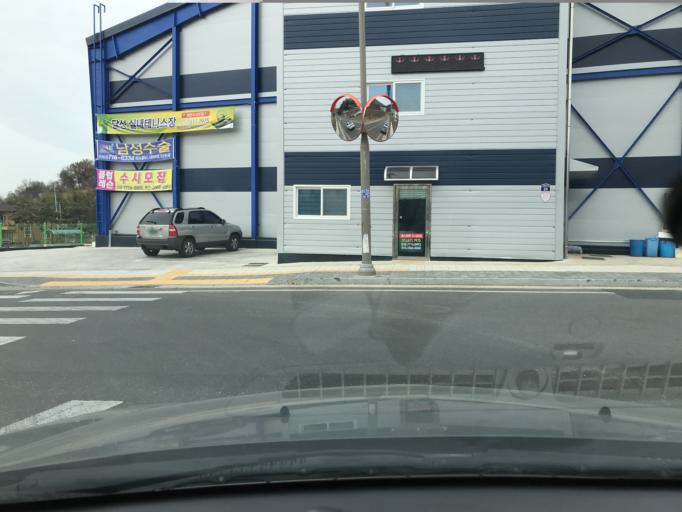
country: KR
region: Daegu
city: Hwawon
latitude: 35.7000
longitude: 128.4524
